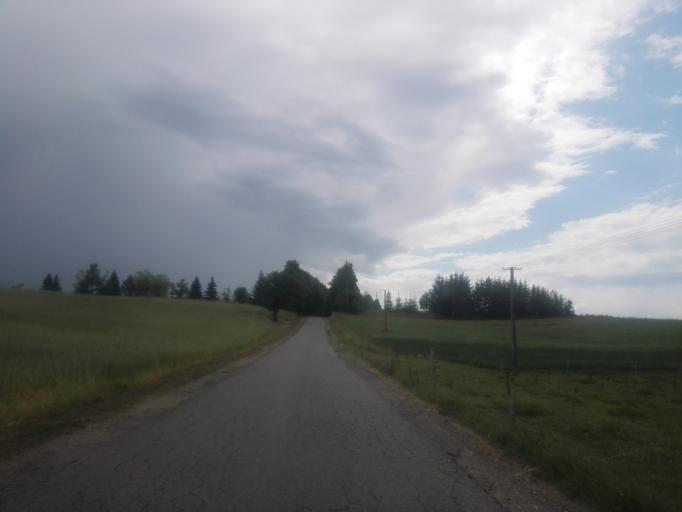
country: PL
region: Podlasie
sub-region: Powiat sejnenski
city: Sejny
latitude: 54.1413
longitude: 23.4213
